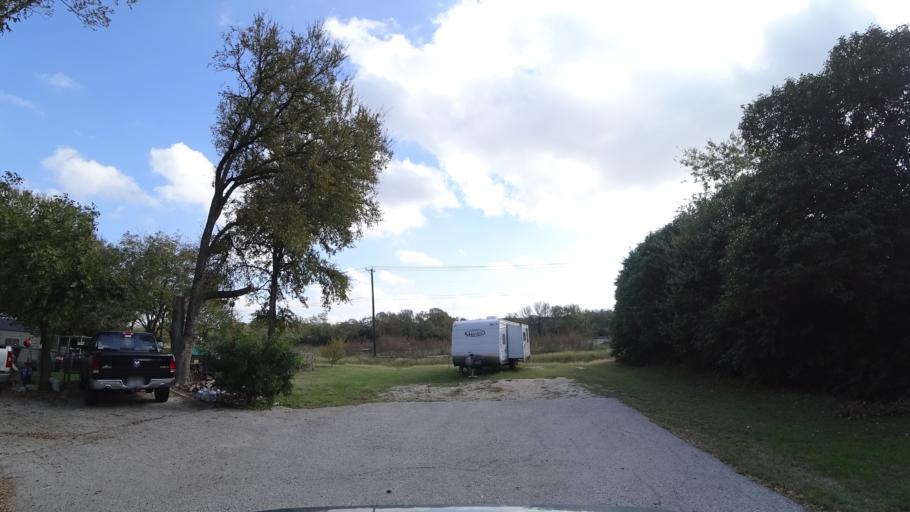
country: US
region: Texas
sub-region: Williamson County
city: Round Rock
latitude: 30.5094
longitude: -97.6733
